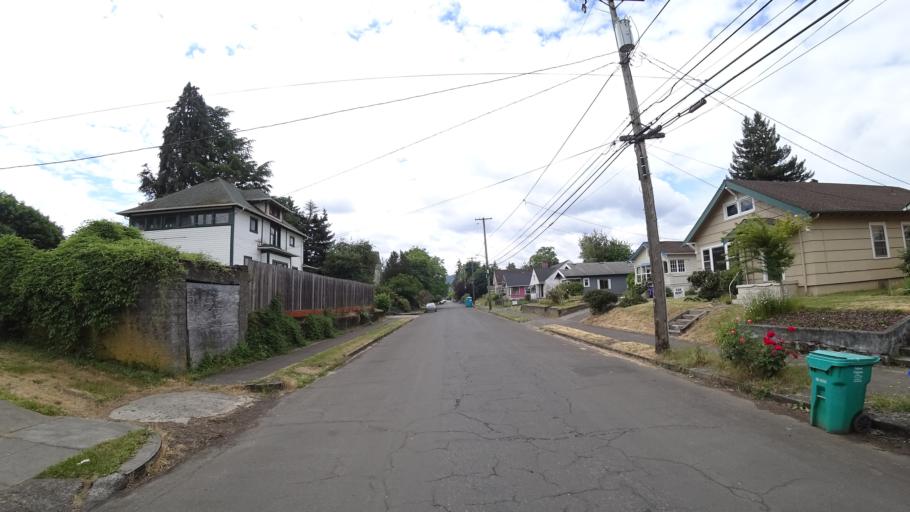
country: US
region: Oregon
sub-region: Multnomah County
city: Portland
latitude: 45.5782
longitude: -122.7200
